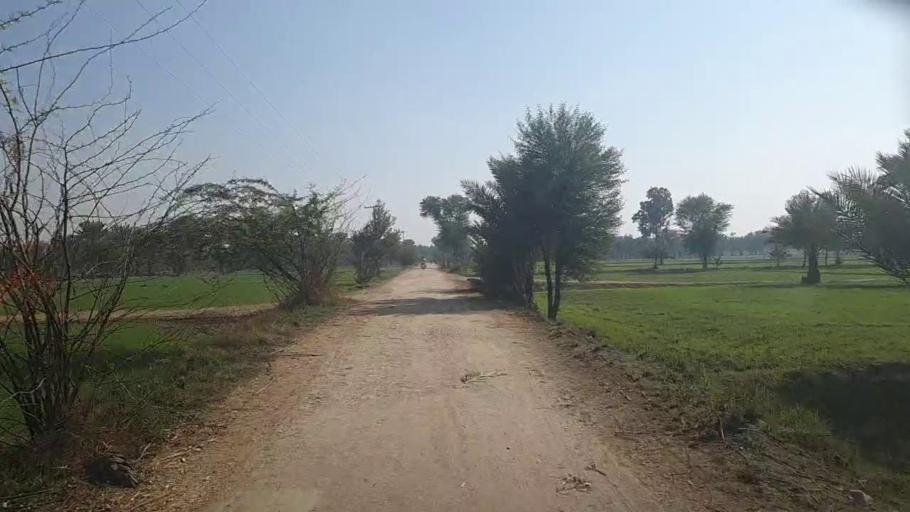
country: PK
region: Sindh
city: Kot Diji
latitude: 27.4347
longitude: 68.7168
